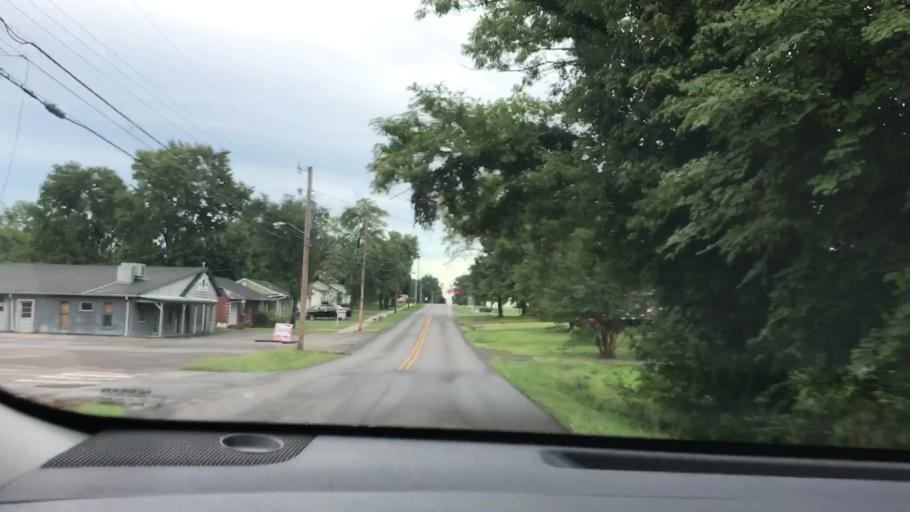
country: US
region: Kentucky
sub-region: Calloway County
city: Murray
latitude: 36.6029
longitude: -88.3190
